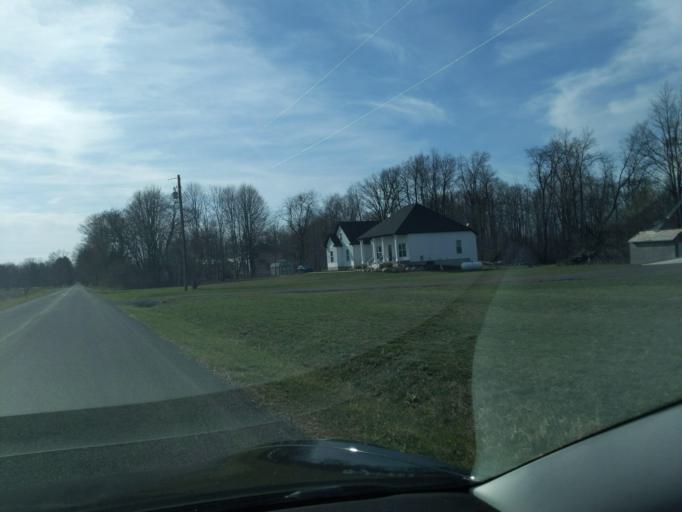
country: US
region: Michigan
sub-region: Ingham County
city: Okemos
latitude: 42.6761
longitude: -84.3693
